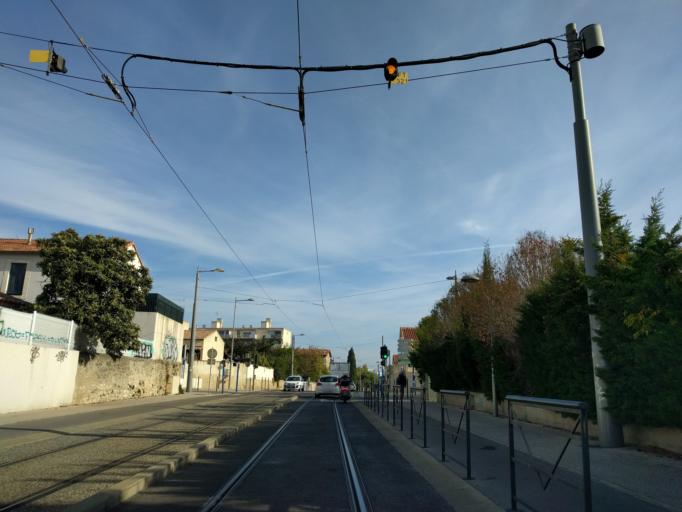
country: FR
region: Languedoc-Roussillon
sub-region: Departement de l'Herault
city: Montpellier
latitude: 43.5918
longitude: 3.8919
